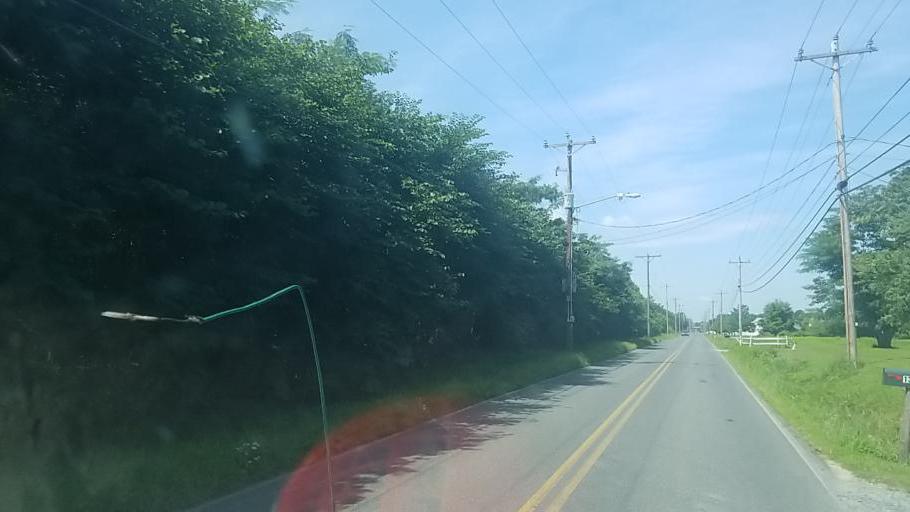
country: US
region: Maryland
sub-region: Caroline County
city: Denton
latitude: 38.8842
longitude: -75.8035
